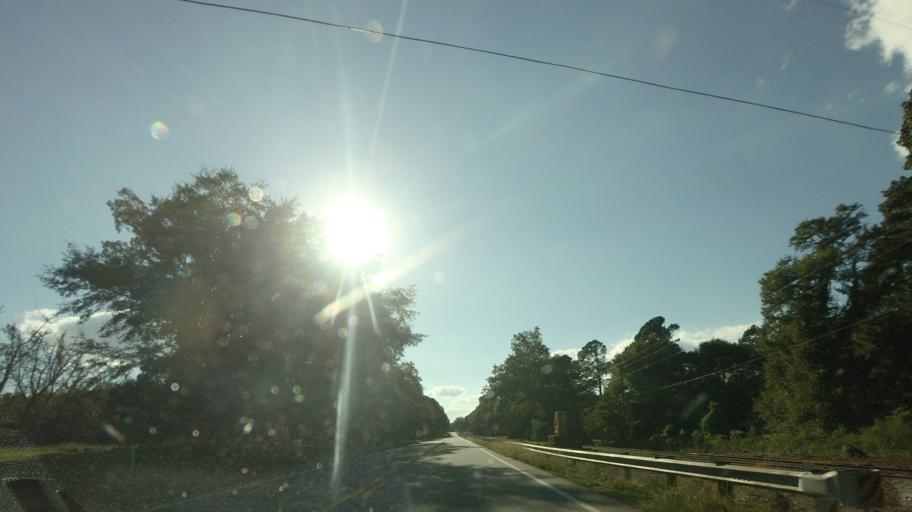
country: US
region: Georgia
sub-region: Lamar County
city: Barnesville
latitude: 32.9648
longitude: -84.2319
